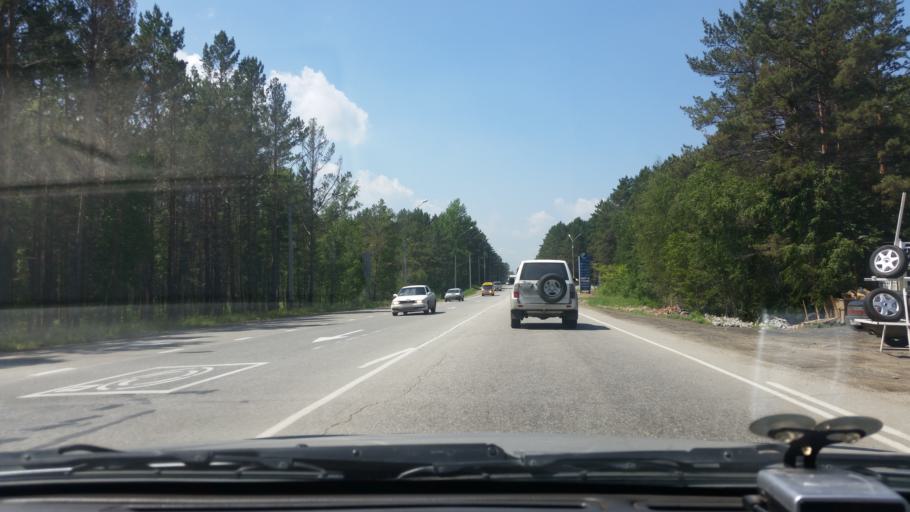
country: RU
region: Irkutsk
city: Shelekhov
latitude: 52.2156
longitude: 104.1228
